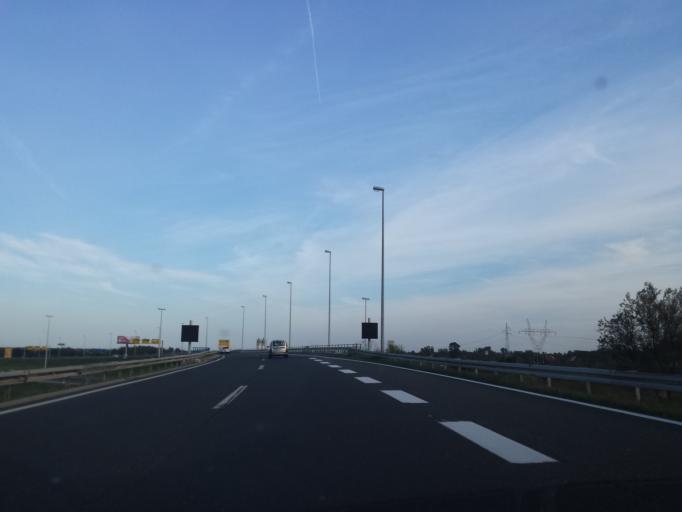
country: HR
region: Grad Zagreb
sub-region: Sesvete
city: Sesvete
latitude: 45.7983
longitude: 16.1361
